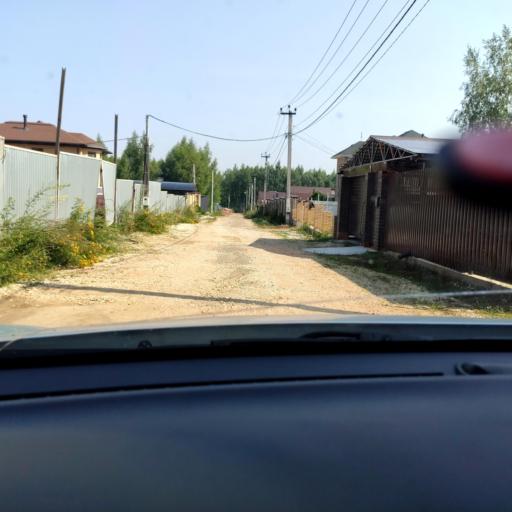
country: RU
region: Tatarstan
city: Stolbishchi
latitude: 55.7385
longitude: 49.2539
